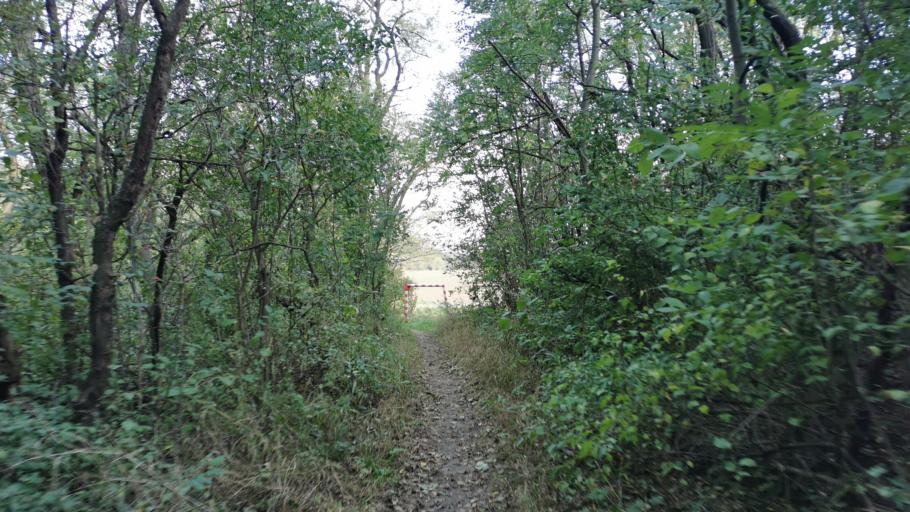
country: SK
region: Trnavsky
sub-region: Okres Skalica
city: Skalica
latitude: 48.8172
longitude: 17.2356
